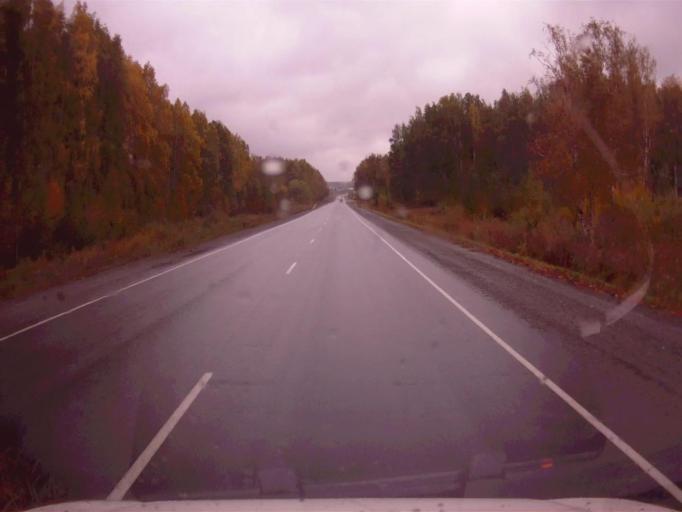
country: RU
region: Chelyabinsk
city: Roshchino
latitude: 55.3635
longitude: 61.2077
